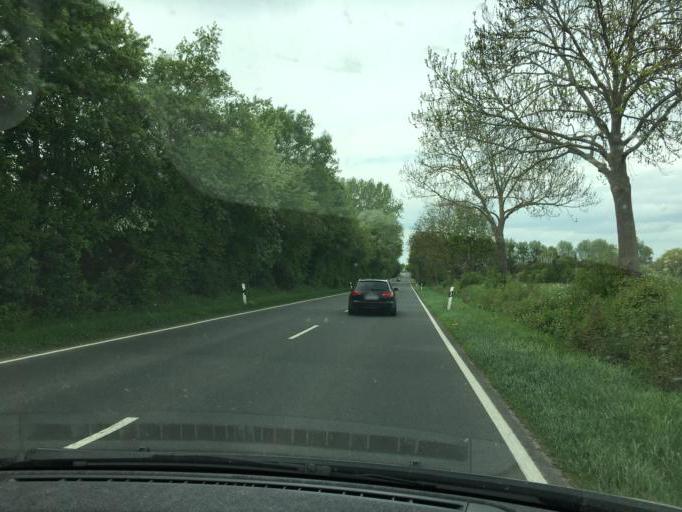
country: DE
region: North Rhine-Westphalia
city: Zulpich
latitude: 50.6987
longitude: 6.7200
